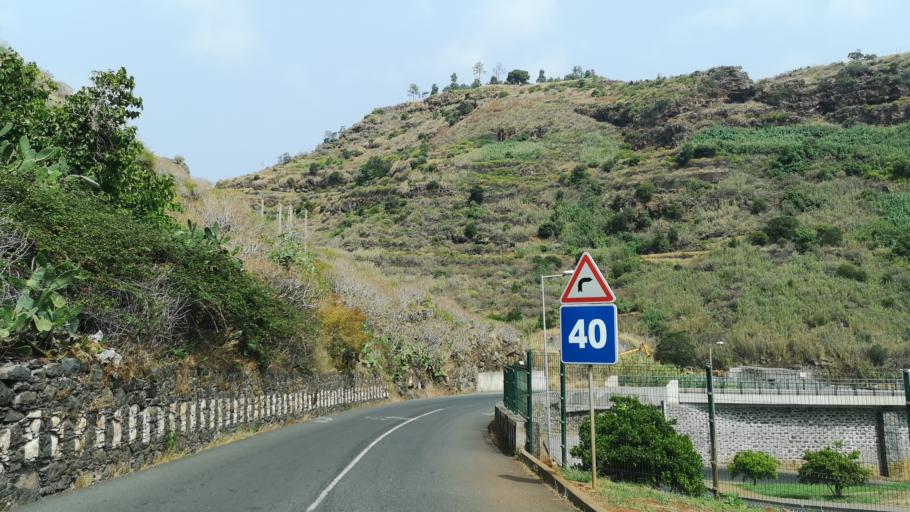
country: PT
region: Madeira
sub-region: Santa Cruz
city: Santa Cruz
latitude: 32.6614
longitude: -16.8131
